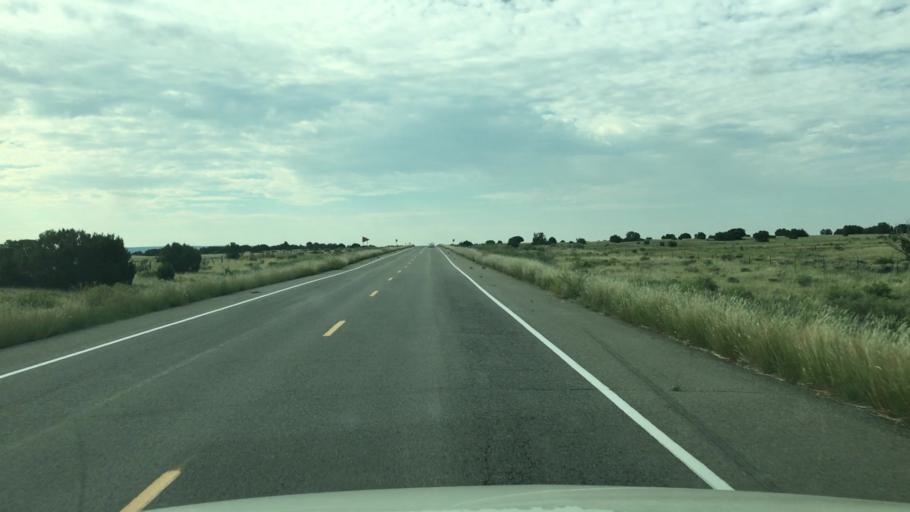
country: US
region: New Mexico
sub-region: Santa Fe County
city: Eldorado at Santa Fe
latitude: 35.4313
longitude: -105.8796
